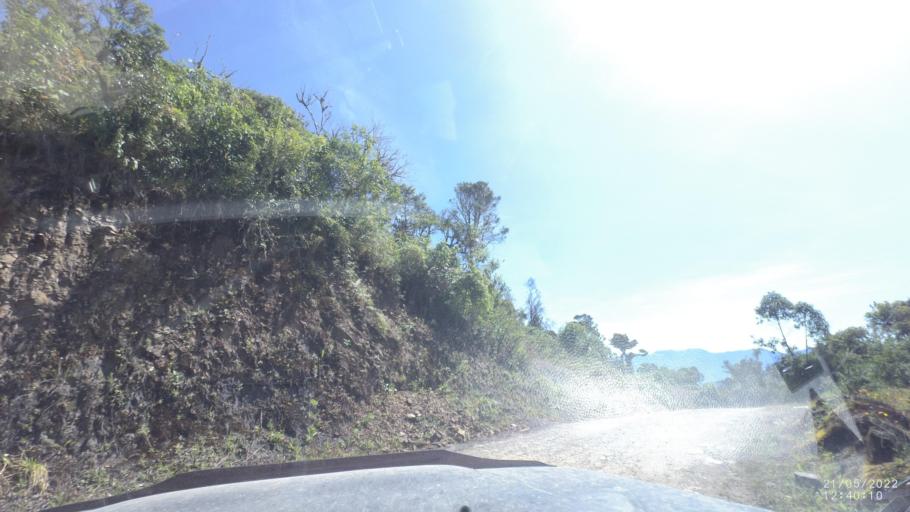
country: BO
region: Cochabamba
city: Colomi
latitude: -17.1975
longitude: -65.9252
